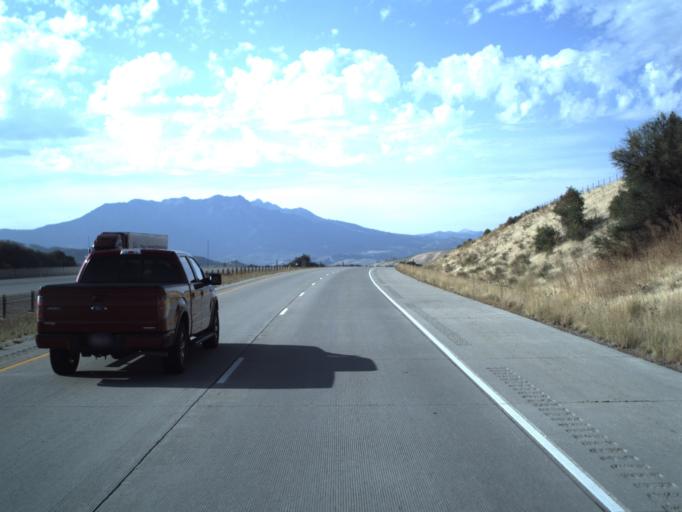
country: US
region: Utah
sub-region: Morgan County
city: Morgan
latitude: 41.0851
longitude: -111.7317
